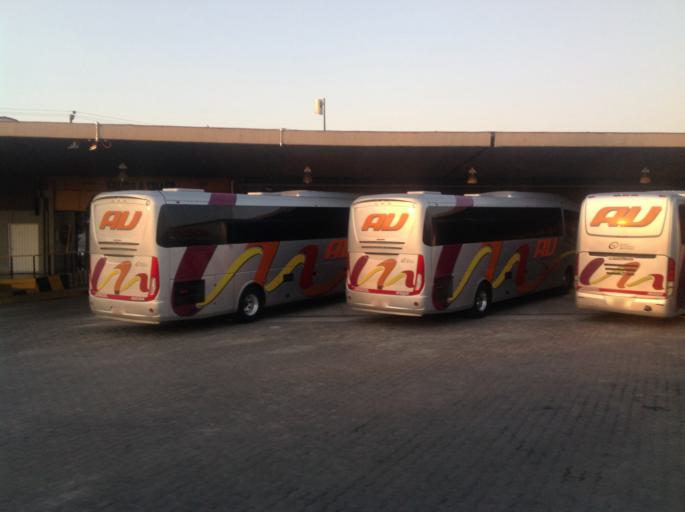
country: MX
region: Mexico City
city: Mexico City
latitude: 19.4310
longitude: -99.1120
